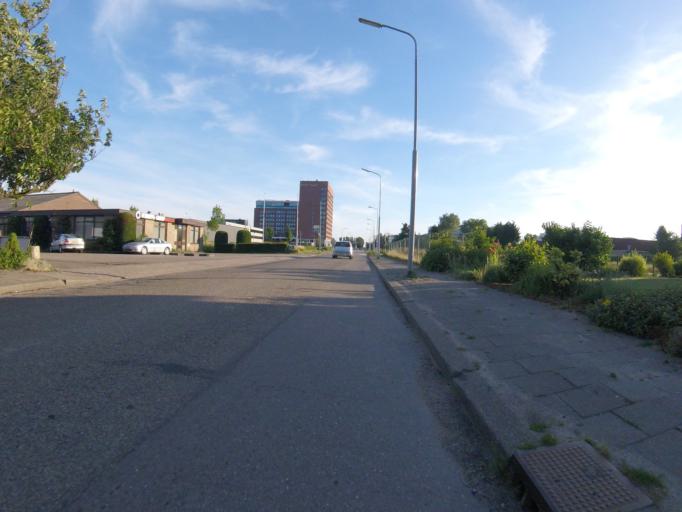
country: NL
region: North Holland
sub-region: Gemeente Haarlemmermeer
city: Hoofddorp
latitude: 52.2954
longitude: 4.7180
